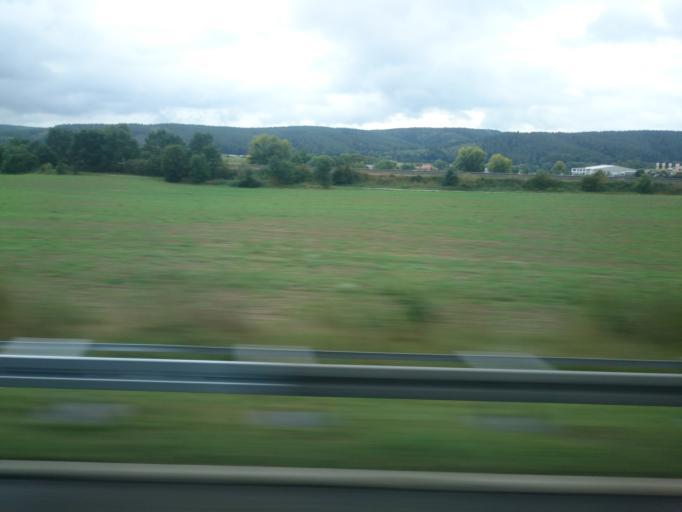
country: DE
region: Thuringia
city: Laasdorf
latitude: 50.8779
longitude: 11.6721
